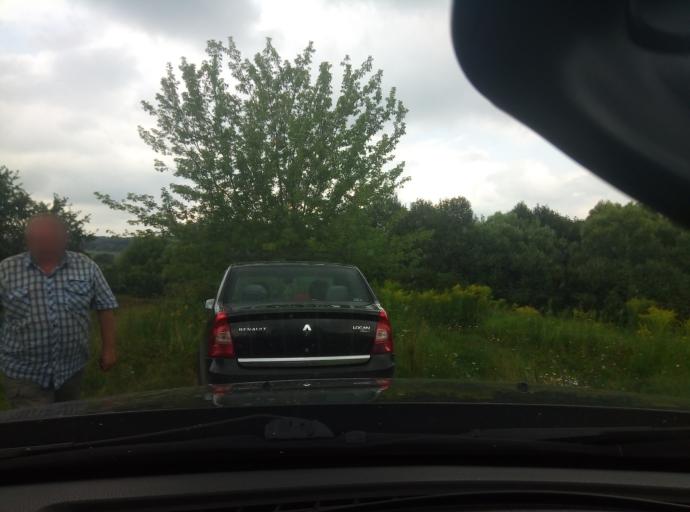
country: RU
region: Tula
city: Shvartsevskiy
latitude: 54.0842
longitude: 38.0199
